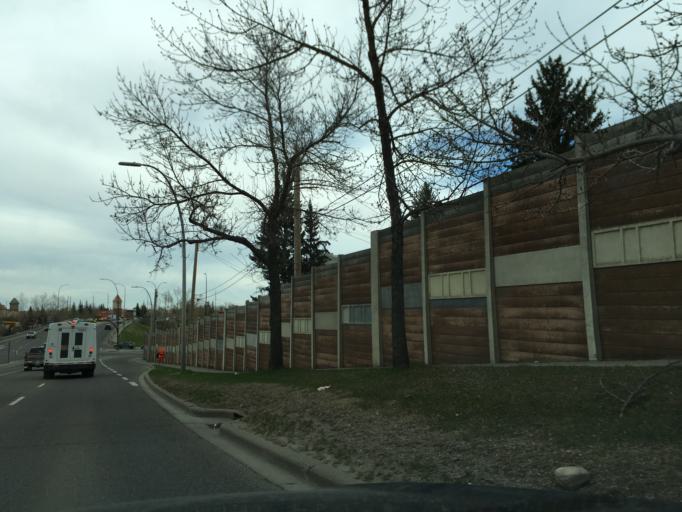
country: CA
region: Alberta
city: Calgary
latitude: 50.9643
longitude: -114.0808
